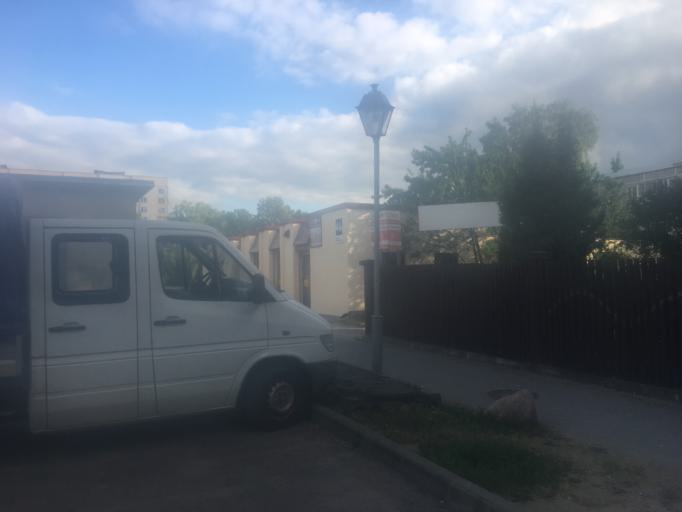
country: BY
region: Grodnenskaya
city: Hrodna
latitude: 53.7020
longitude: 23.8057
